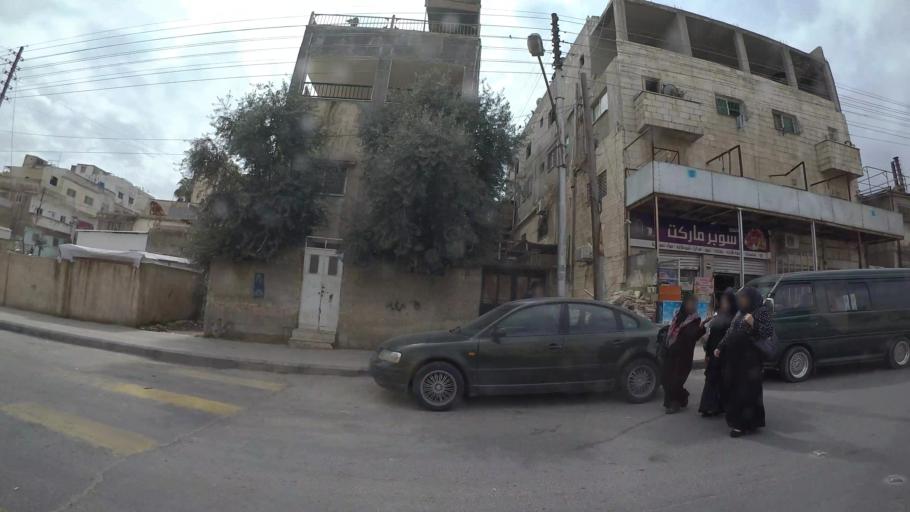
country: JO
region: Amman
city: Amman
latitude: 31.9621
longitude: 35.9532
